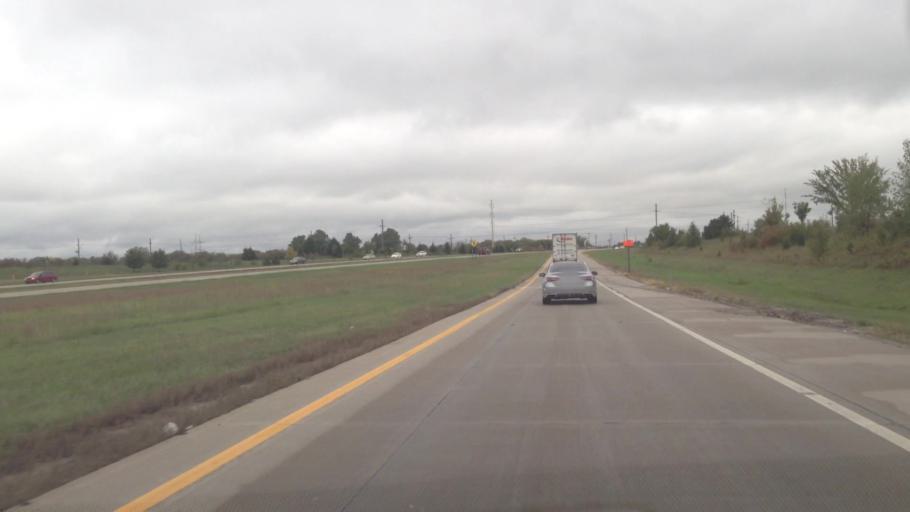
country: US
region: Kansas
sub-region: Johnson County
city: Olathe
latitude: 38.9279
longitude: -94.8516
